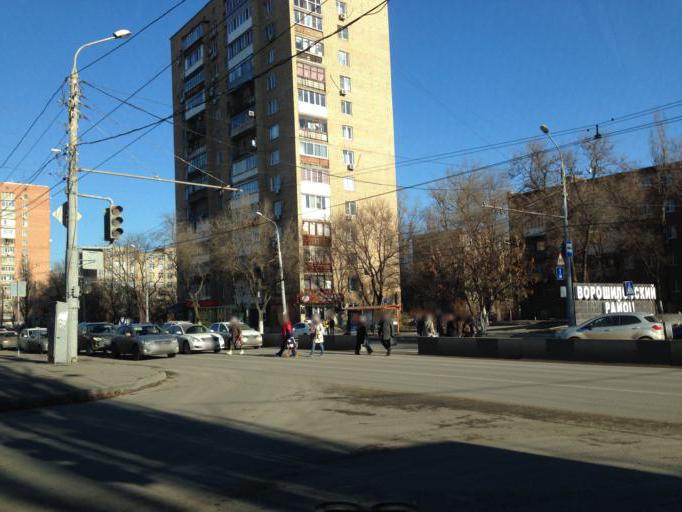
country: RU
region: Rostov
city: Rostov-na-Donu
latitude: 47.2455
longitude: 39.7128
